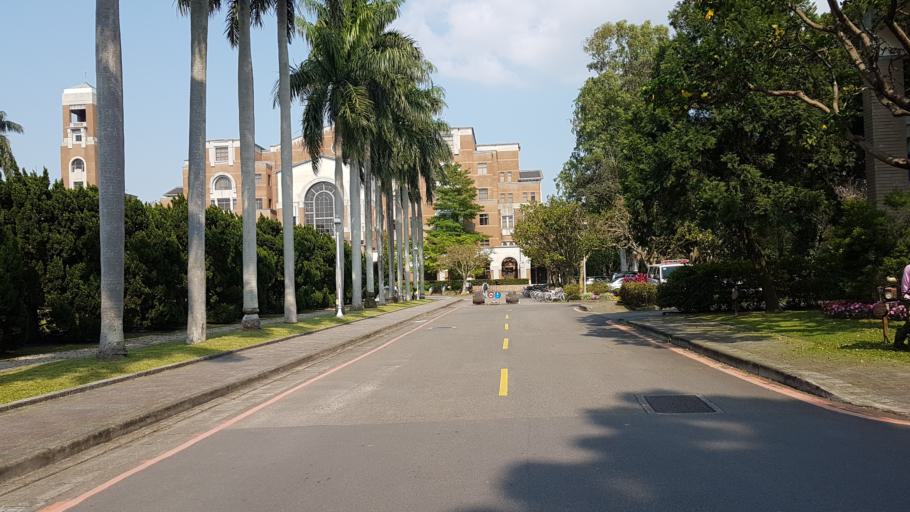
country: TW
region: Taipei
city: Taipei
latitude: 25.0170
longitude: 121.5394
